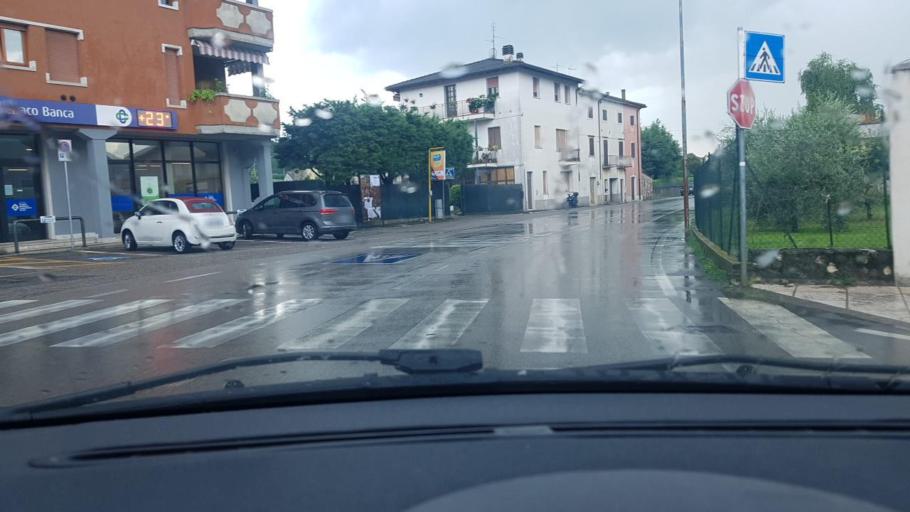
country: IT
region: Veneto
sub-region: Provincia di Verona
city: Caprino Veronese
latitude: 45.6014
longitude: 10.7951
